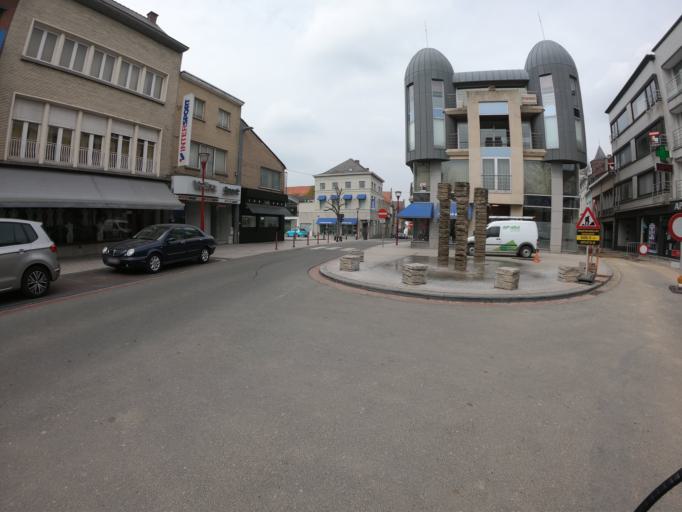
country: BE
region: Flanders
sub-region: Provincie Oost-Vlaanderen
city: Ronse
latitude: 50.7472
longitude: 3.5991
